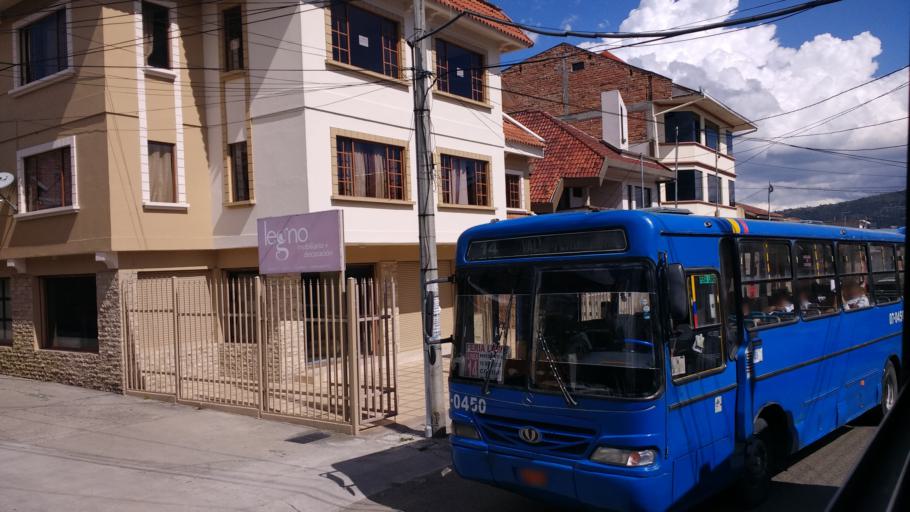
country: EC
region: Azuay
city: Cuenca
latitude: -2.9011
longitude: -79.0236
